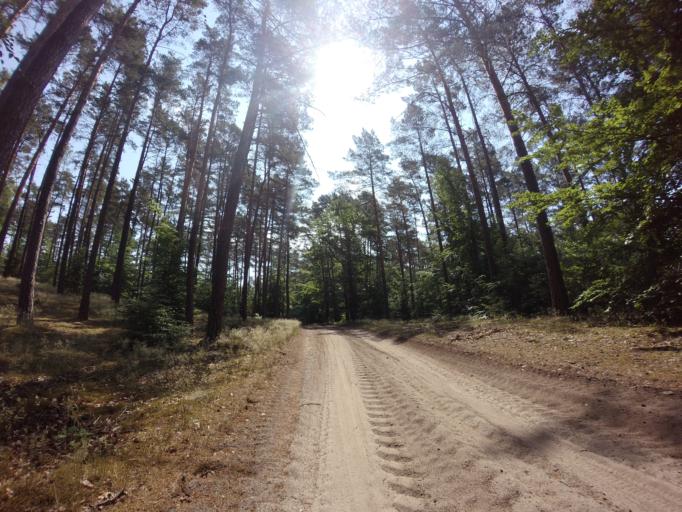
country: PL
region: West Pomeranian Voivodeship
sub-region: Powiat choszczenski
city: Bierzwnik
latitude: 53.0910
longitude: 15.7465
